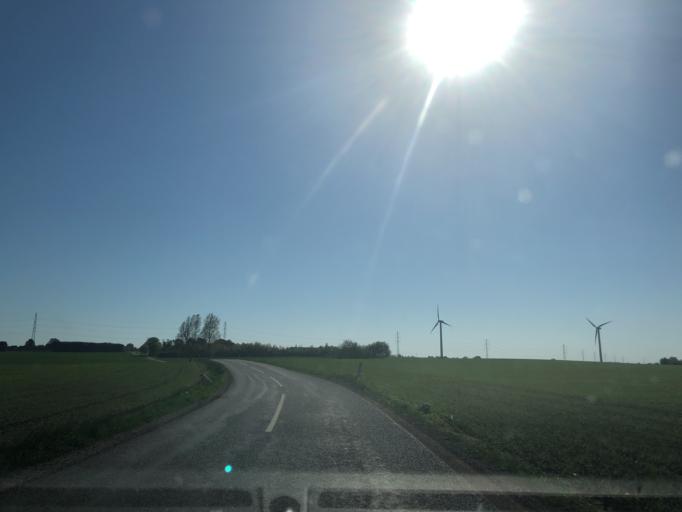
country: DK
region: Zealand
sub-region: Ringsted Kommune
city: Ringsted
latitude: 55.4681
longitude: 11.7445
